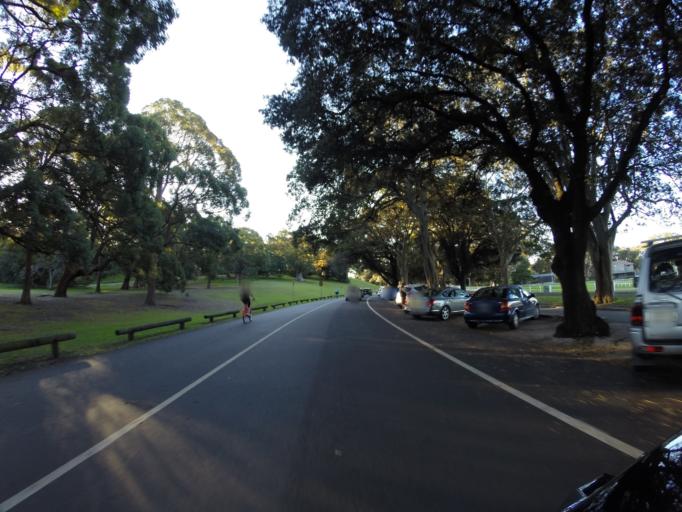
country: AU
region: New South Wales
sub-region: Woollahra
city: Woollahra
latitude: -33.9000
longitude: 151.2277
